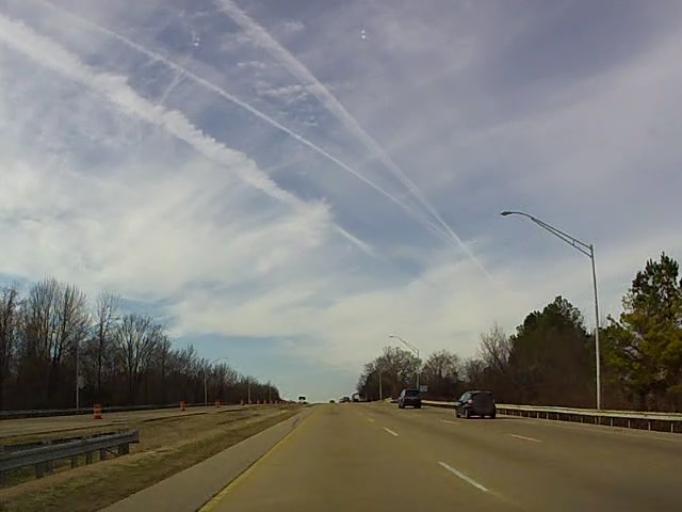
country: US
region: Tennessee
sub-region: Shelby County
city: Bartlett
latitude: 35.1469
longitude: -89.9006
